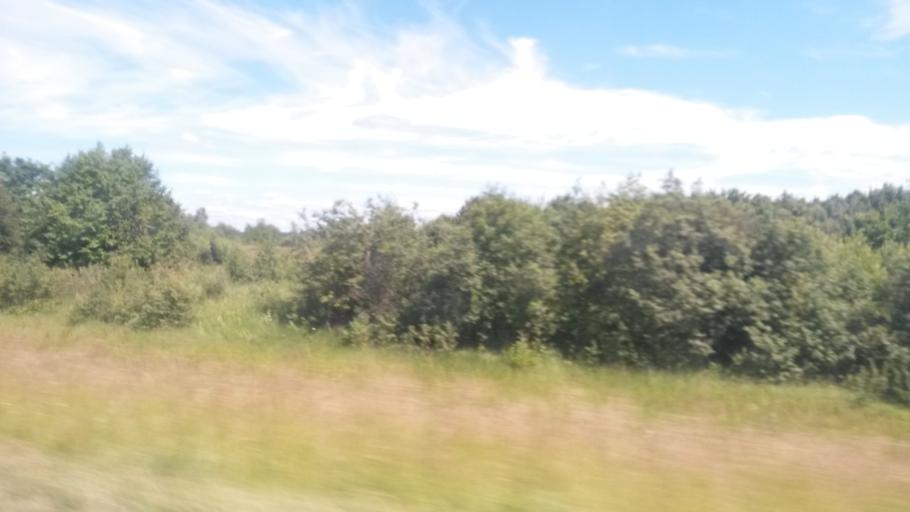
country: RU
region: Ivanovo
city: Staraya Vichuga
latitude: 57.2240
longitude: 41.8625
